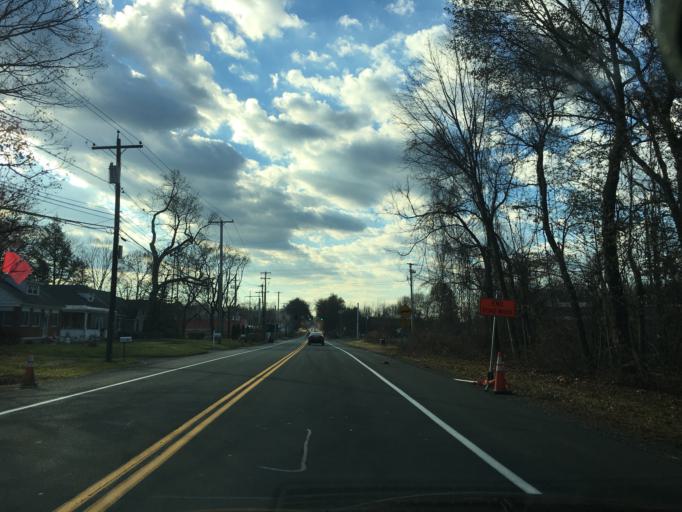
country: US
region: New York
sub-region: Albany County
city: Menands
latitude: 42.6742
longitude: -73.6913
